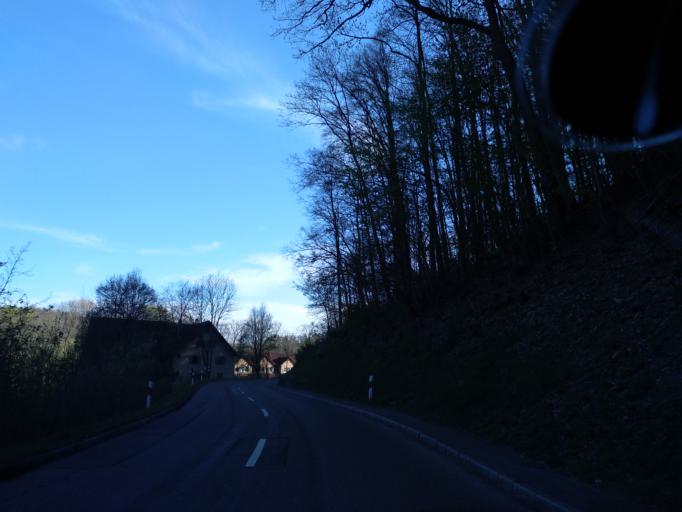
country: DE
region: Baden-Wuerttemberg
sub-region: Regierungsbezirk Stuttgart
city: Kirchberg an der Jagst
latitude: 49.2071
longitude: 9.9904
